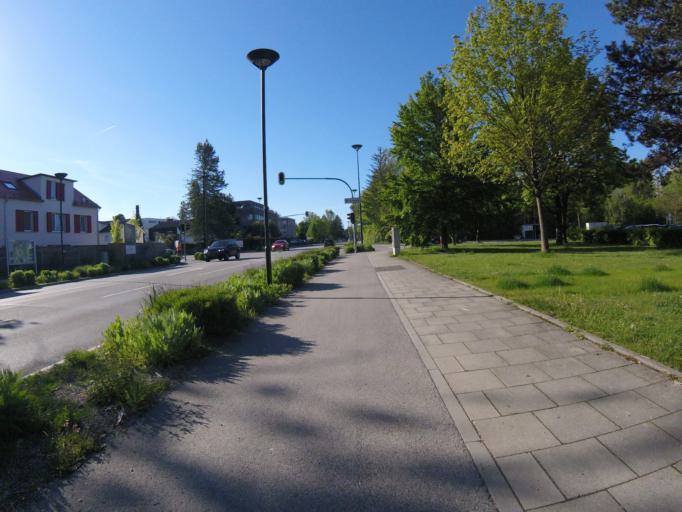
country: DE
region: Bavaria
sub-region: Upper Bavaria
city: Ottobrunn
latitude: 48.0551
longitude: 11.6680
